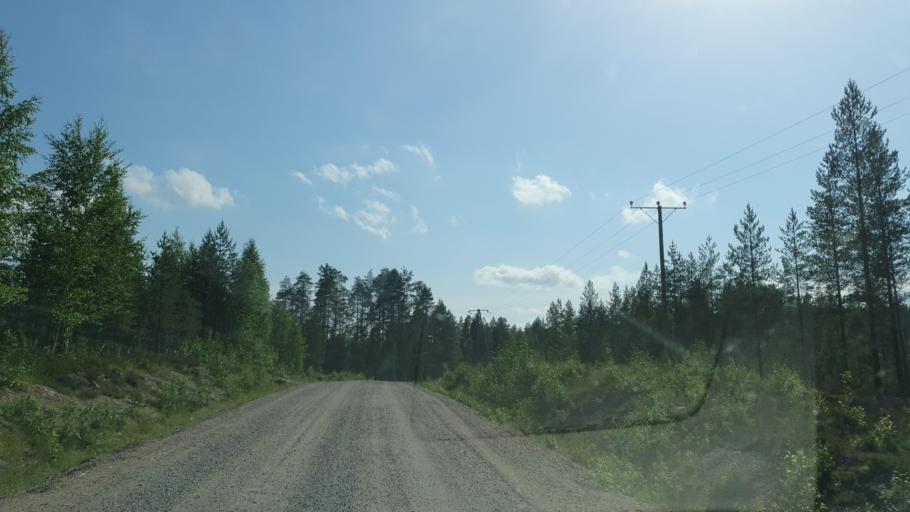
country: FI
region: Kainuu
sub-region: Kehys-Kainuu
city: Kuhmo
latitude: 64.0187
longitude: 29.9132
